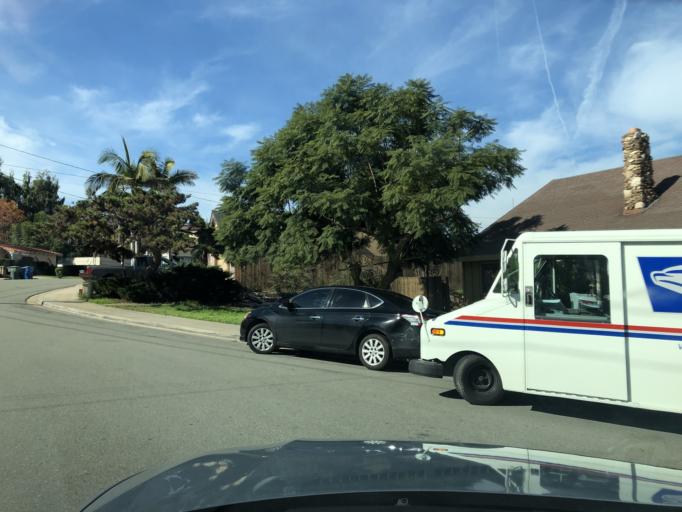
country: US
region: California
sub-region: San Diego County
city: Chula Vista
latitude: 32.6463
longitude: -117.0667
